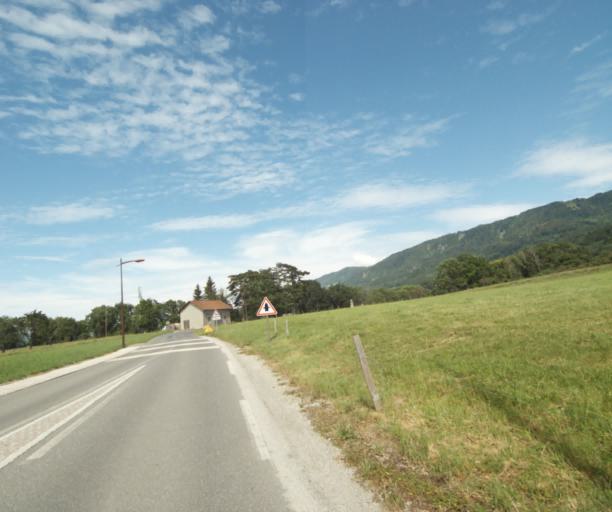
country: FR
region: Rhone-Alpes
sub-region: Departement de la Haute-Savoie
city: Bons-en-Chablais
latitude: 46.2780
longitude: 6.4159
